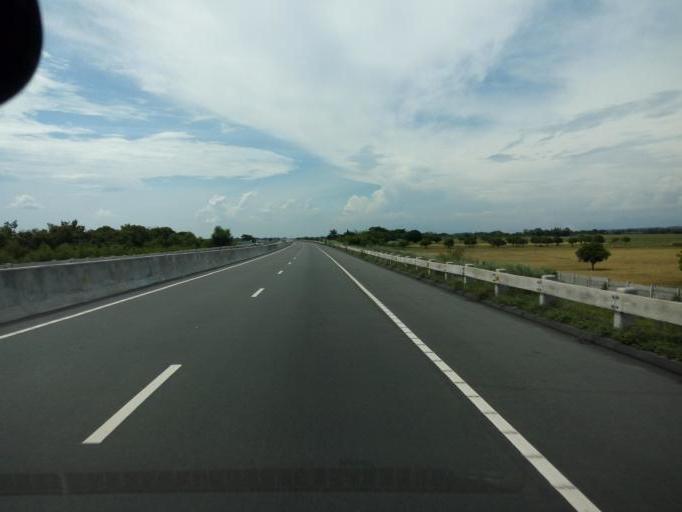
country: PH
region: Central Luzon
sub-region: Province of Nueva Ecija
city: Calancuasan Norte
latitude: 15.8043
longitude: 120.6394
